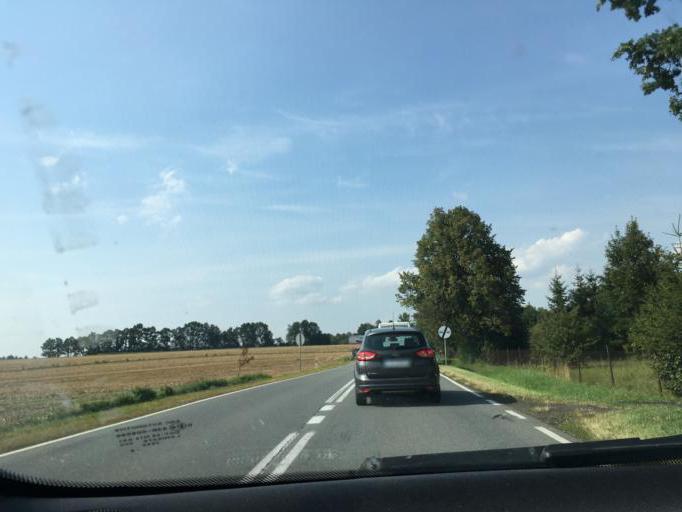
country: PL
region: Opole Voivodeship
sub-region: Powiat prudnicki
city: Laka Prudnicka
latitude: 50.3668
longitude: 17.5389
